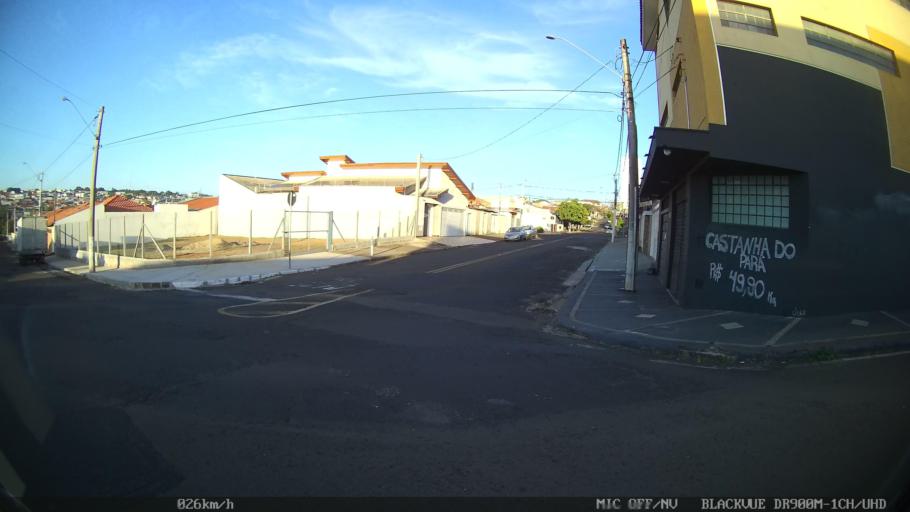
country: BR
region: Sao Paulo
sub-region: Franca
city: Franca
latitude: -20.5219
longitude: -47.3944
